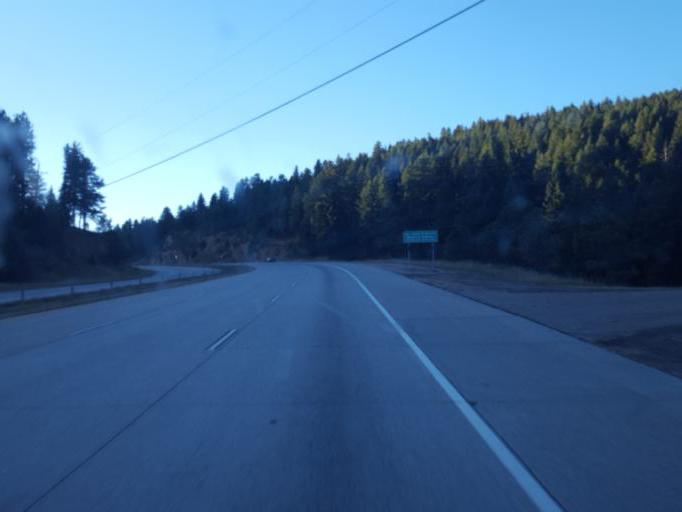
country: US
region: Colorado
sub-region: Jefferson County
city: Indian Hills
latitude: 39.6041
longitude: -105.2295
